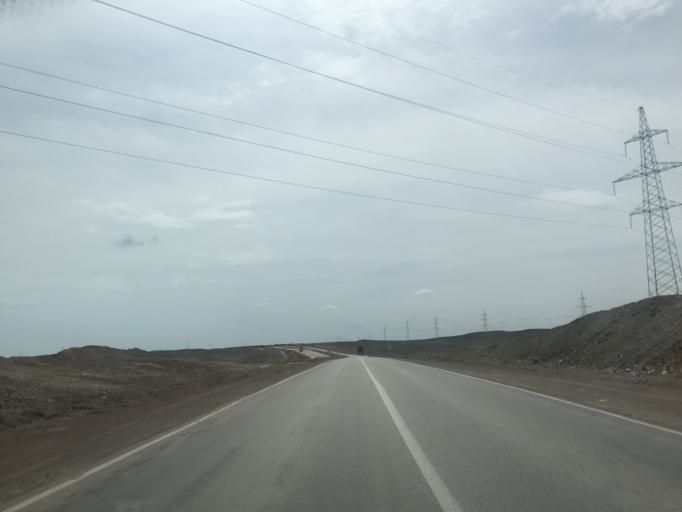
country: KZ
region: Zhambyl
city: Mynaral
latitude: 45.3509
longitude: 73.6876
